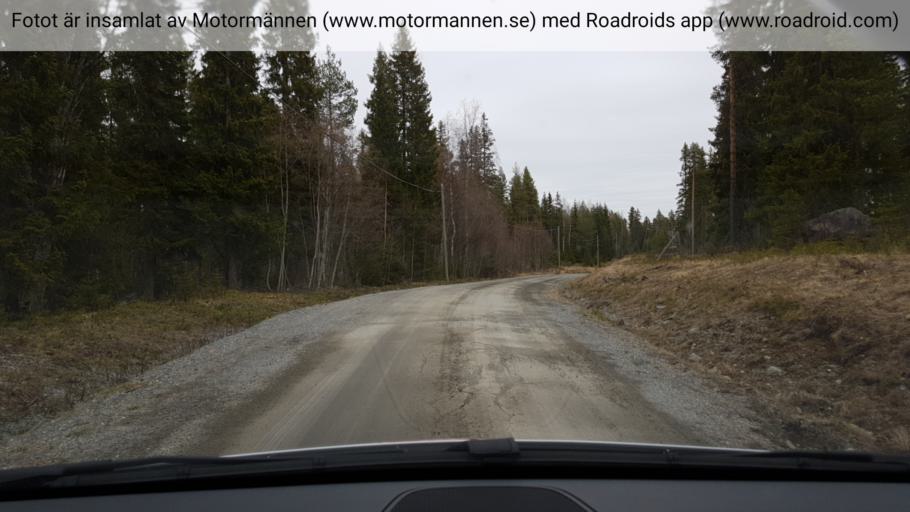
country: SE
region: Jaemtland
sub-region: Bergs Kommun
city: Hoverberg
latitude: 62.8508
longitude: 14.5424
